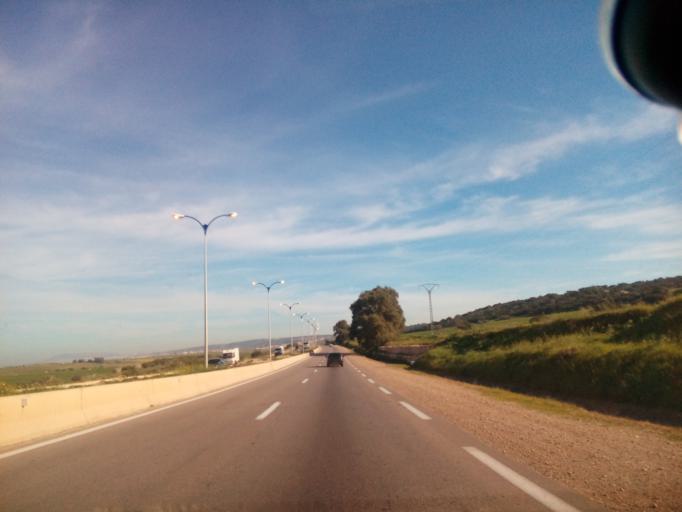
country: DZ
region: Mostaganem
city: Mostaganem
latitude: 35.8118
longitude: -0.0343
